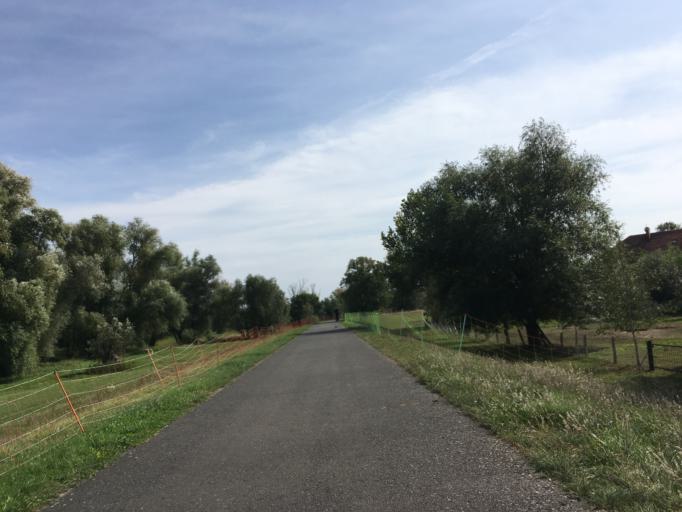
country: DE
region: Brandenburg
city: Neuzelle
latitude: 52.0689
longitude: 14.7550
